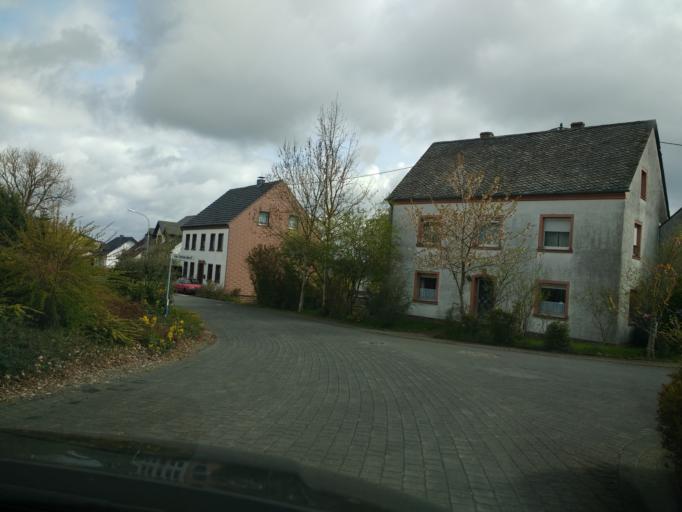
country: DE
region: Rheinland-Pfalz
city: Birresborn
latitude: 50.2118
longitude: 6.6089
